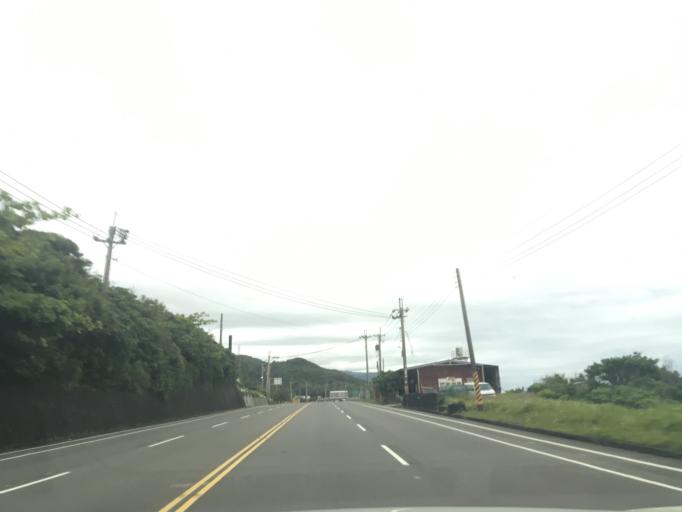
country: TW
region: Taiwan
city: Hengchun
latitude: 22.3007
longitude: 120.8888
